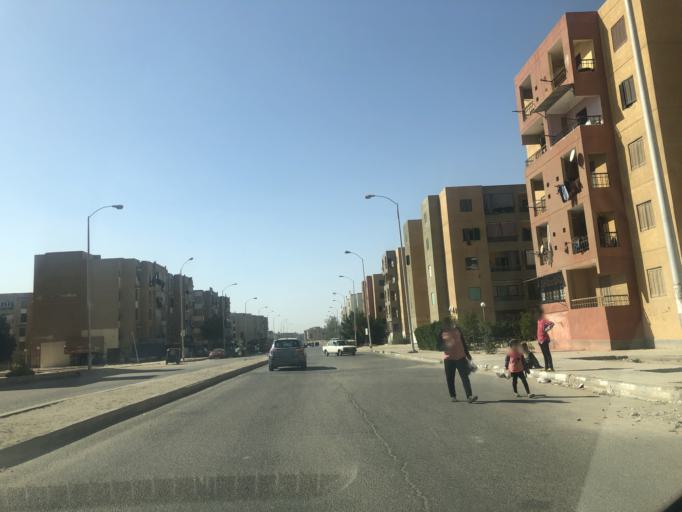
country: EG
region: Al Jizah
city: Madinat Sittah Uktubar
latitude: 29.9245
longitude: 30.9326
